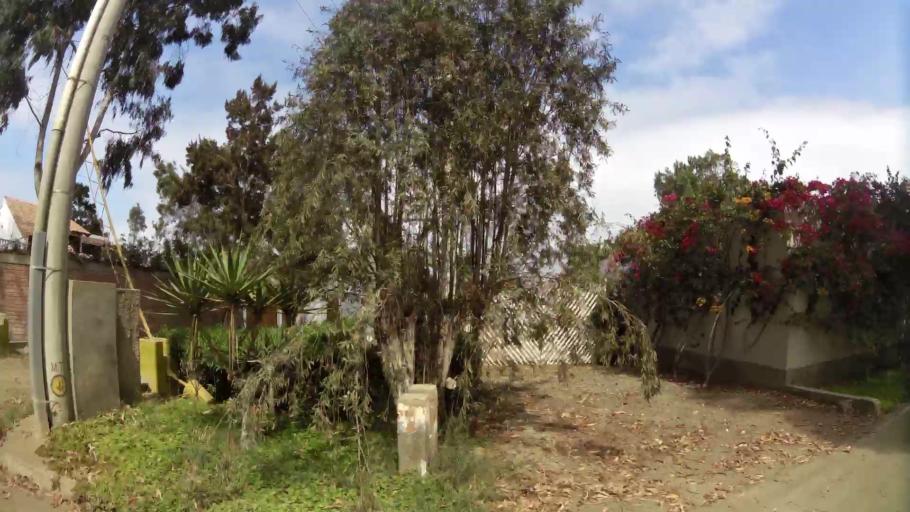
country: PE
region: Lima
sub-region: Provincia de Canete
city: Mala
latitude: -12.7326
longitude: -76.6280
